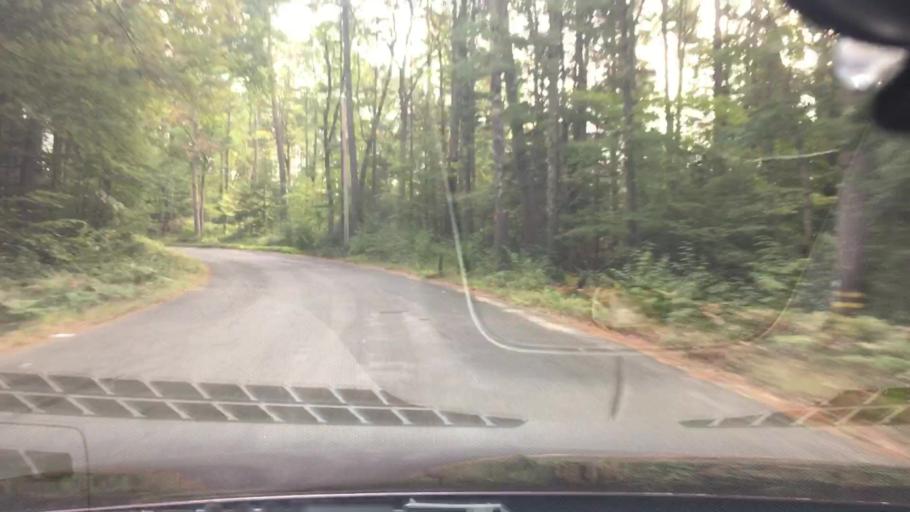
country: US
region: Connecticut
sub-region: Tolland County
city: Stafford
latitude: 41.9952
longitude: -72.3265
